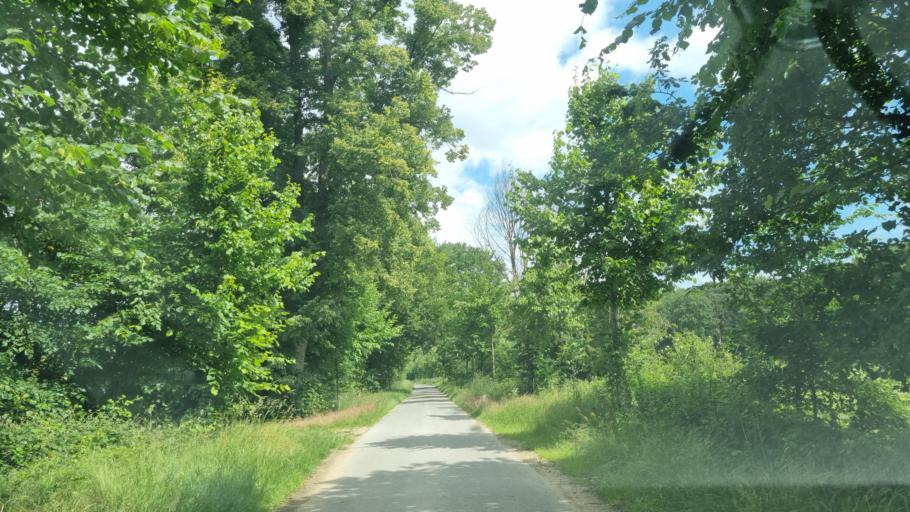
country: DE
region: North Rhine-Westphalia
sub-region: Regierungsbezirk Dusseldorf
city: Kleve
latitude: 51.8027
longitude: 6.1085
